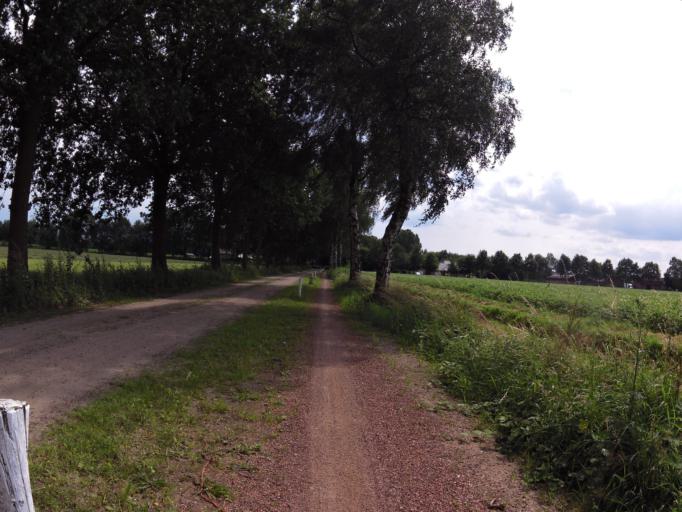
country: NL
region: North Brabant
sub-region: Gemeente Sint-Oedenrode
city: Sint-Oedenrode
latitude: 51.5797
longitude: 5.4676
